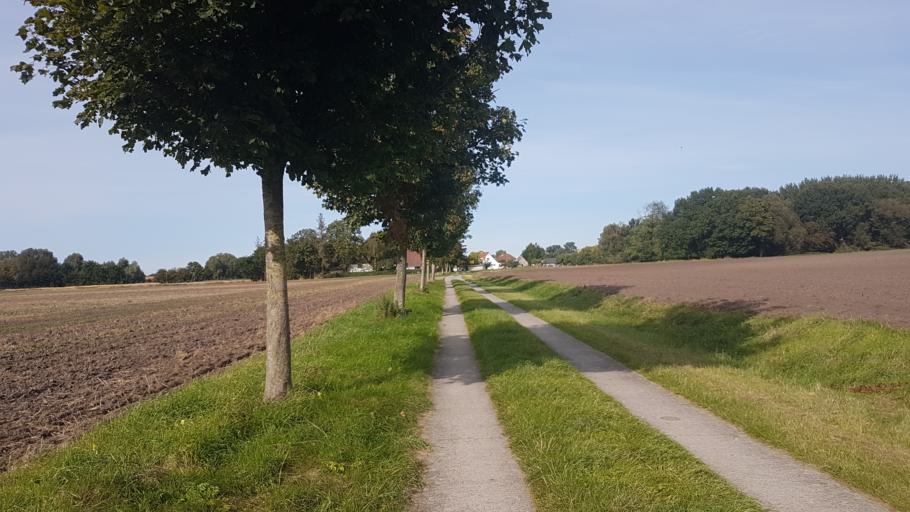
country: DE
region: Mecklenburg-Vorpommern
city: Gingst
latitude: 54.4447
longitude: 13.1834
